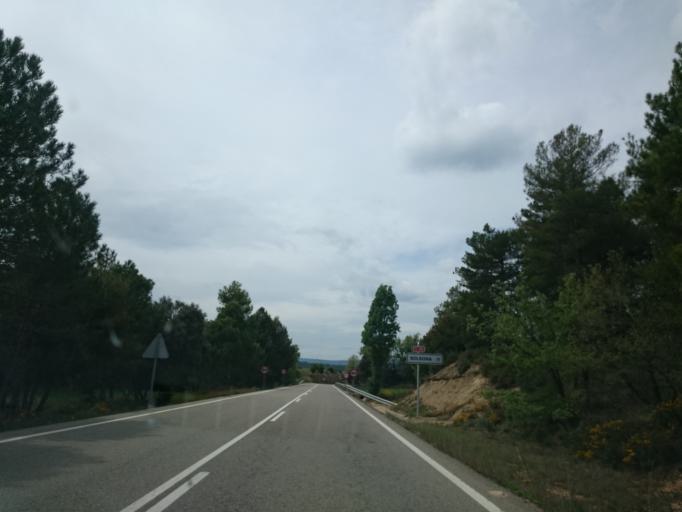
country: ES
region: Catalonia
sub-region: Provincia de Lleida
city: Olius
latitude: 41.9918
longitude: 1.6278
